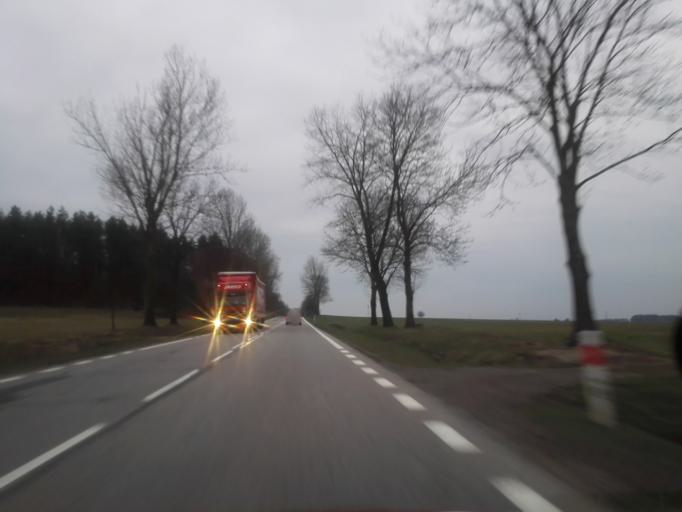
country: PL
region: Podlasie
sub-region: Powiat lomzynski
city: Piatnica
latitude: 53.2691
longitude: 22.1304
